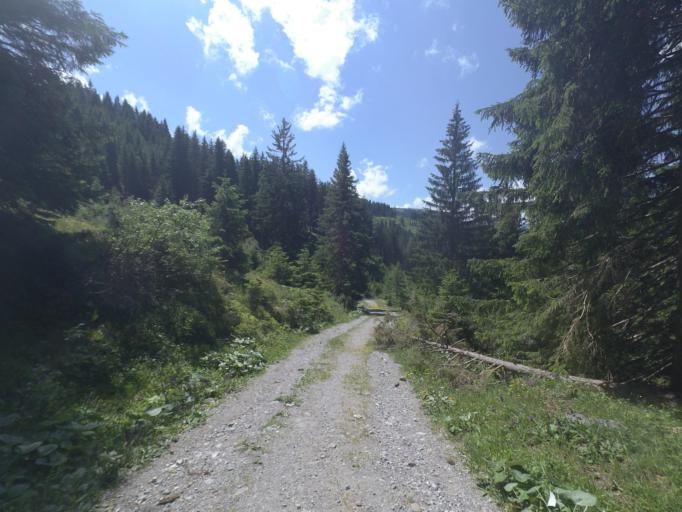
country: AT
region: Salzburg
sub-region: Politischer Bezirk Zell am See
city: Dienten am Hochkonig
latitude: 47.4125
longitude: 13.0021
